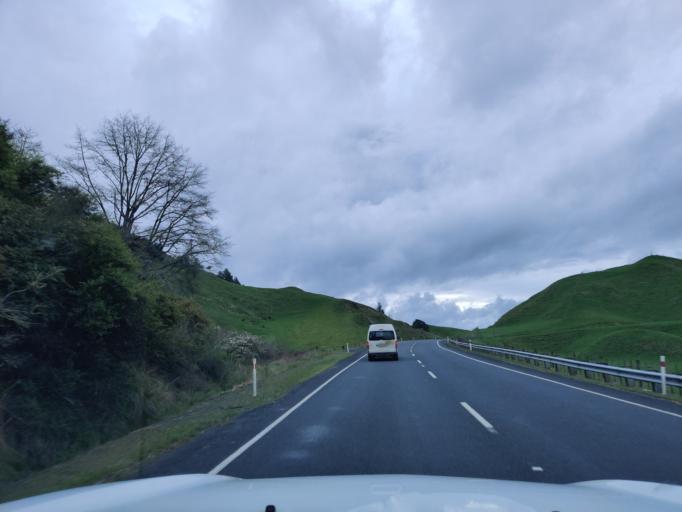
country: NZ
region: Waikato
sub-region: Otorohanga District
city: Otorohanga
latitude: -38.4688
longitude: 175.1697
